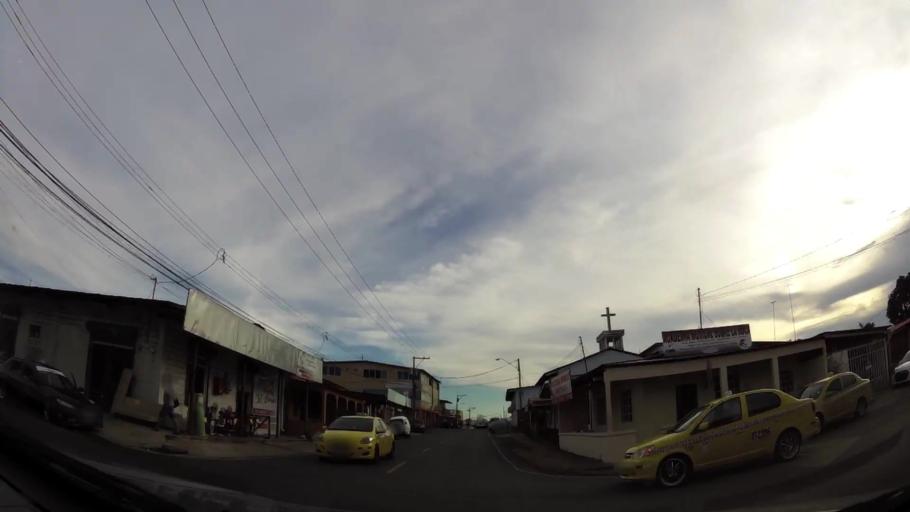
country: PA
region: Panama
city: La Chorrera
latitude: 8.8839
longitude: -79.7798
